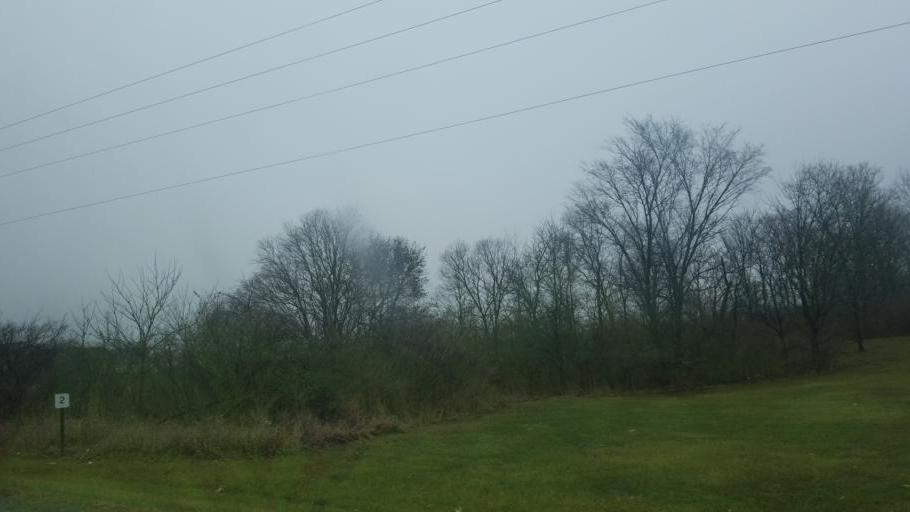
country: US
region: Ohio
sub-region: Champaign County
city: North Lewisburg
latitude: 40.2538
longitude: -83.5801
